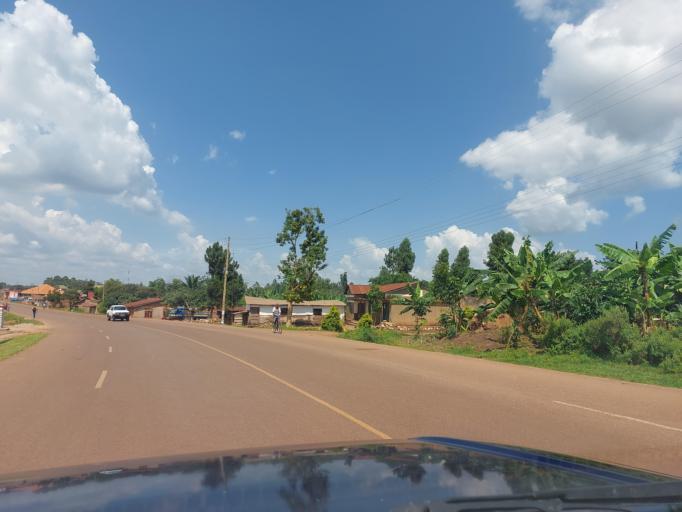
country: UG
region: Central Region
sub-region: Buikwe District
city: Njeru
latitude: 0.3875
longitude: 33.1651
